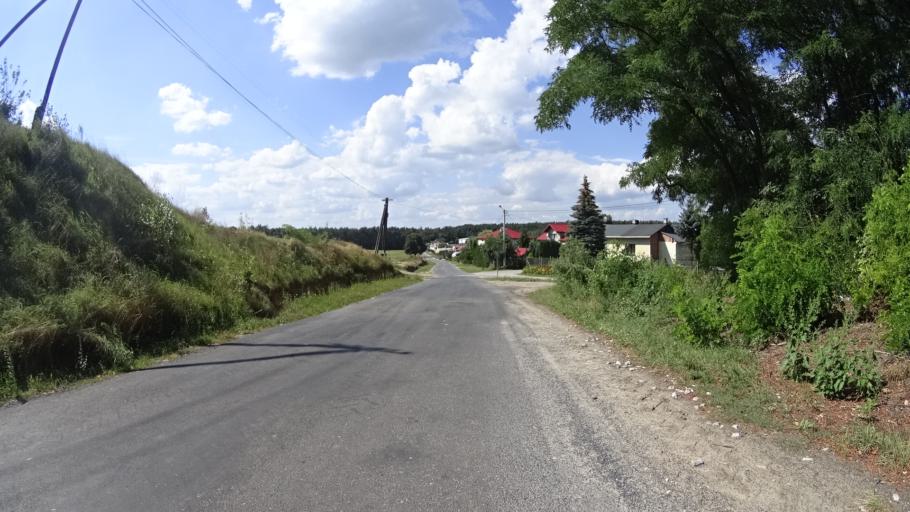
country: PL
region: Masovian Voivodeship
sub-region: Powiat grojecki
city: Mogielnica
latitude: 51.6899
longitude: 20.7483
